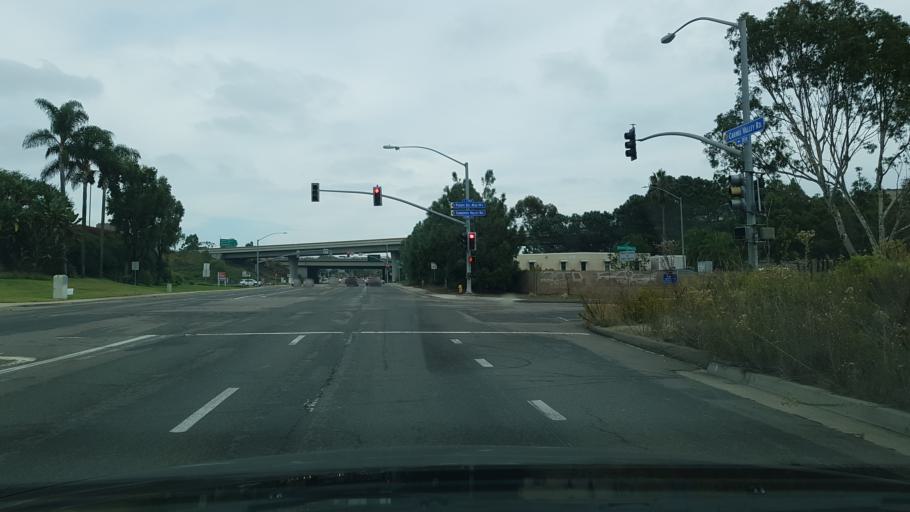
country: US
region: California
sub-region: San Diego County
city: Del Mar
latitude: 32.9312
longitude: -117.2433
